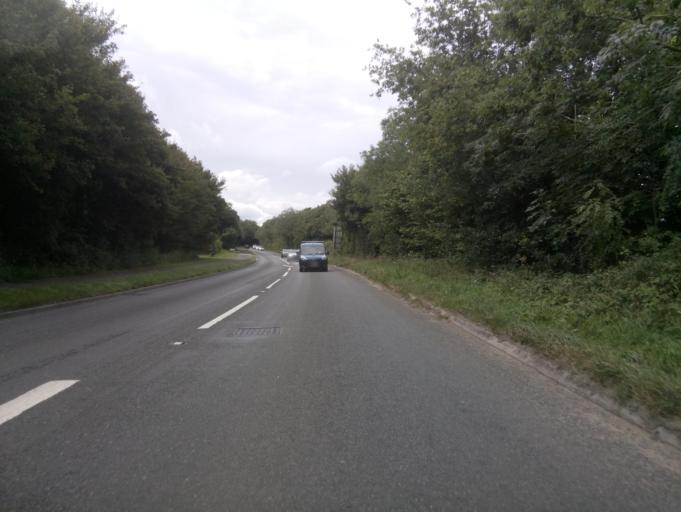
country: GB
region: England
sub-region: Somerset
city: Yeovil
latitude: 50.9175
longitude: -2.6313
